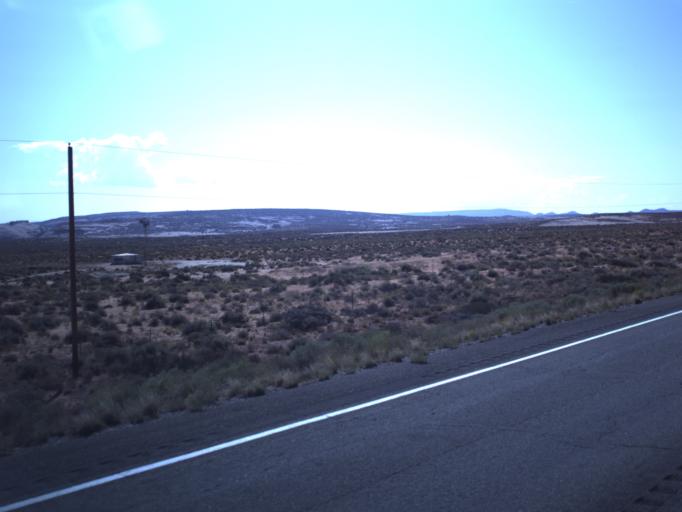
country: US
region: Utah
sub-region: San Juan County
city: Blanding
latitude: 37.0827
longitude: -109.5480
